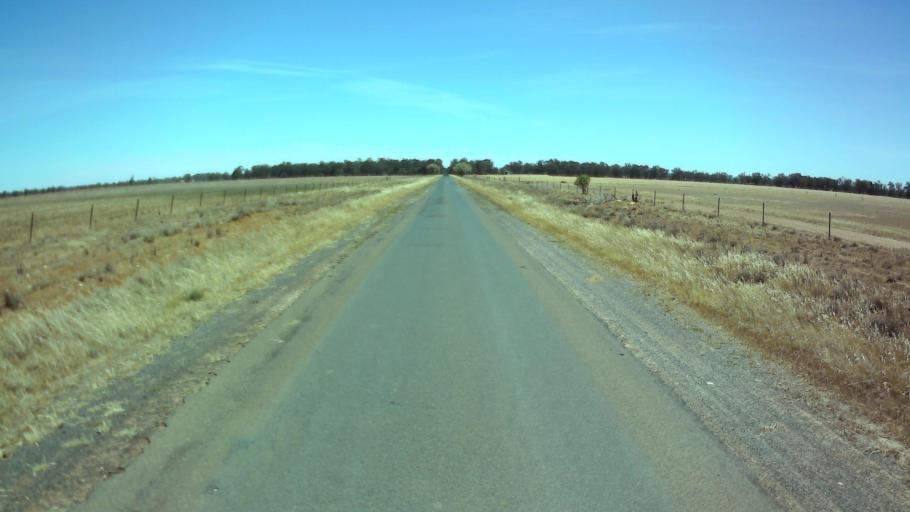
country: AU
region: New South Wales
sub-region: Weddin
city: Grenfell
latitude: -33.8599
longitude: 147.6939
